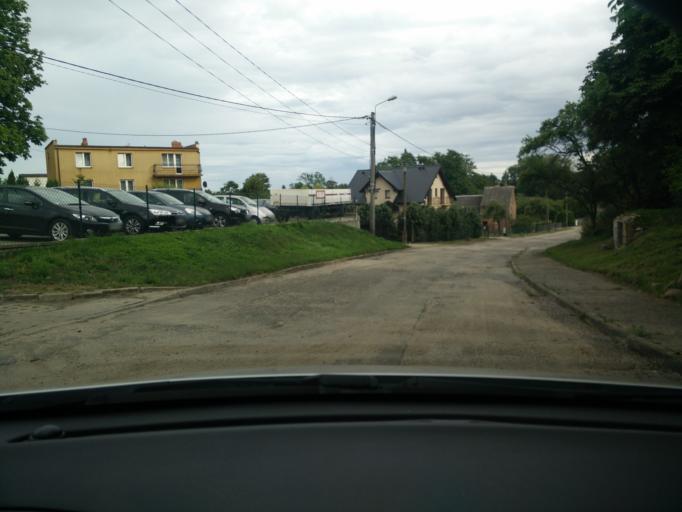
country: PL
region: Pomeranian Voivodeship
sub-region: Powiat pucki
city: Mrzezino
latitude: 54.6680
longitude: 18.4558
